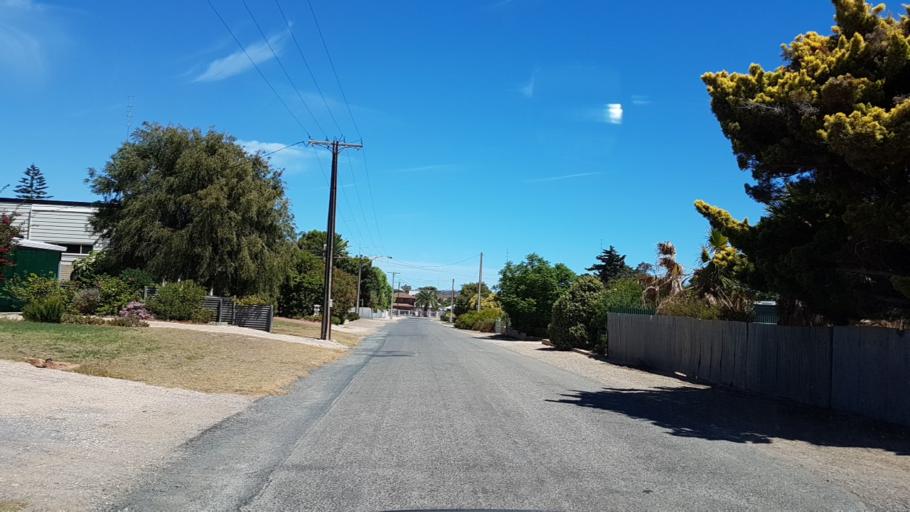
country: AU
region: South Australia
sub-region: Copper Coast
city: Wallaroo
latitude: -34.0579
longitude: 137.5612
